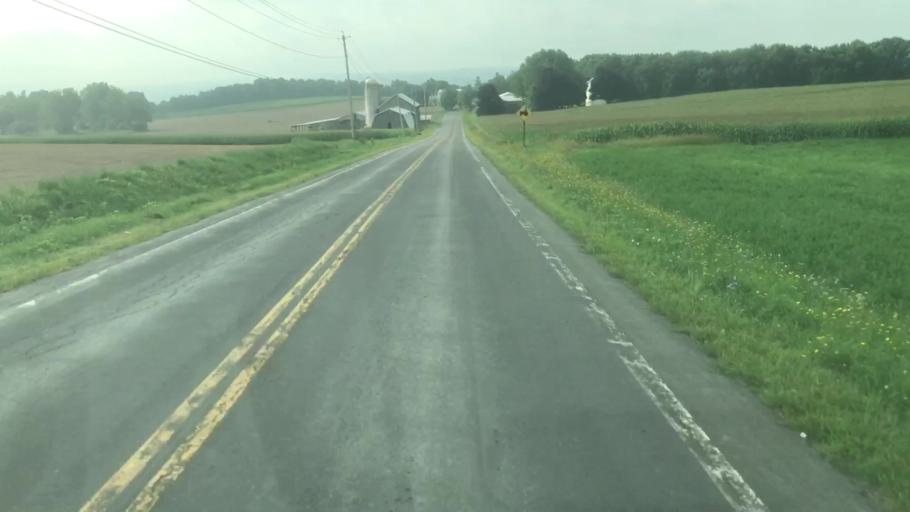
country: US
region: New York
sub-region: Onondaga County
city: Skaneateles
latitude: 42.8789
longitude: -76.4466
